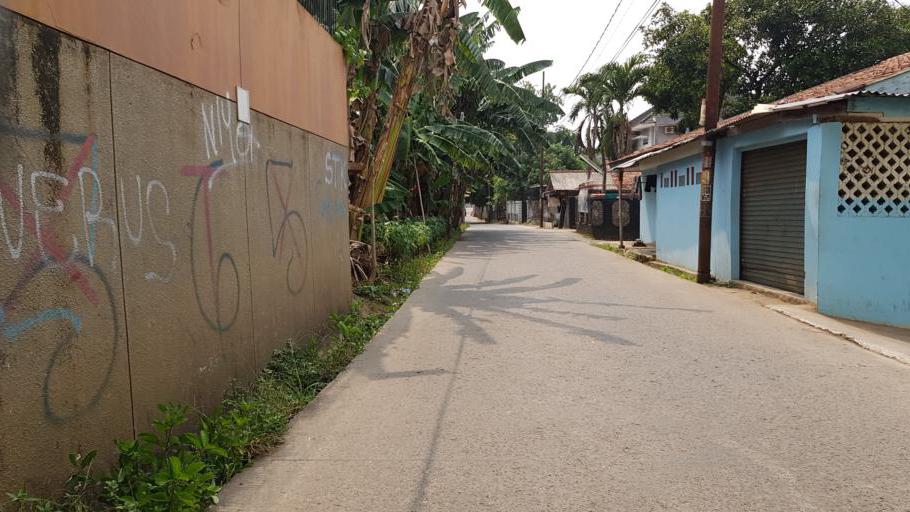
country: ID
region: West Java
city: Pamulang
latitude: -6.3314
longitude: 106.7969
